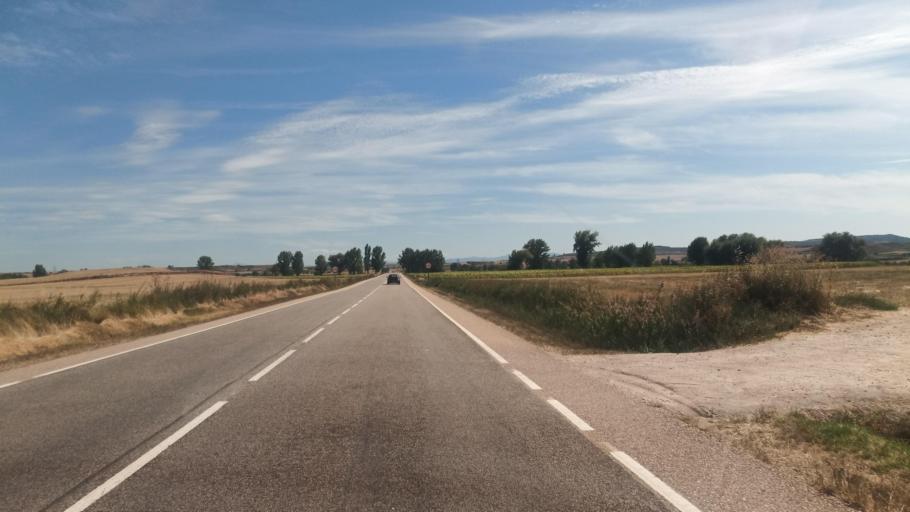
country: ES
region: Castille and Leon
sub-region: Provincia de Burgos
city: Quintanabureba
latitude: 42.6028
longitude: -3.3500
